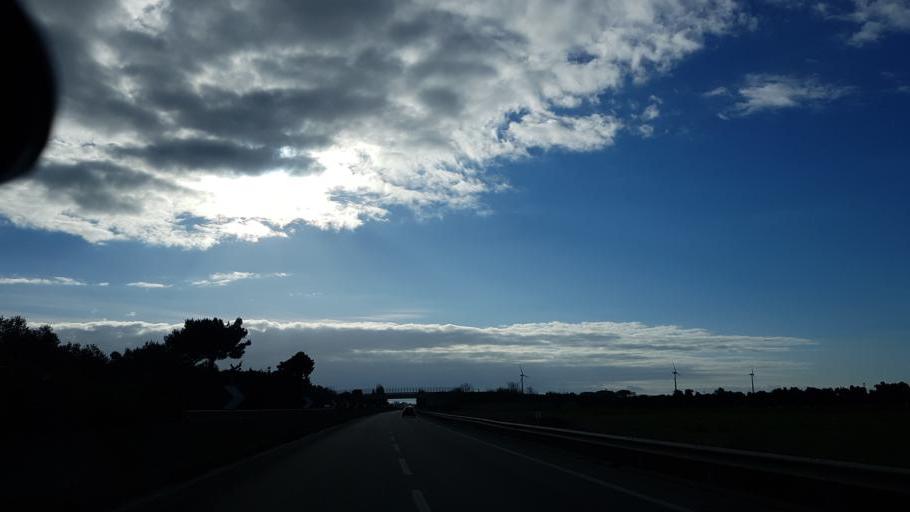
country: IT
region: Apulia
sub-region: Provincia di Brindisi
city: La Rosa
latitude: 40.5795
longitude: 17.9787
